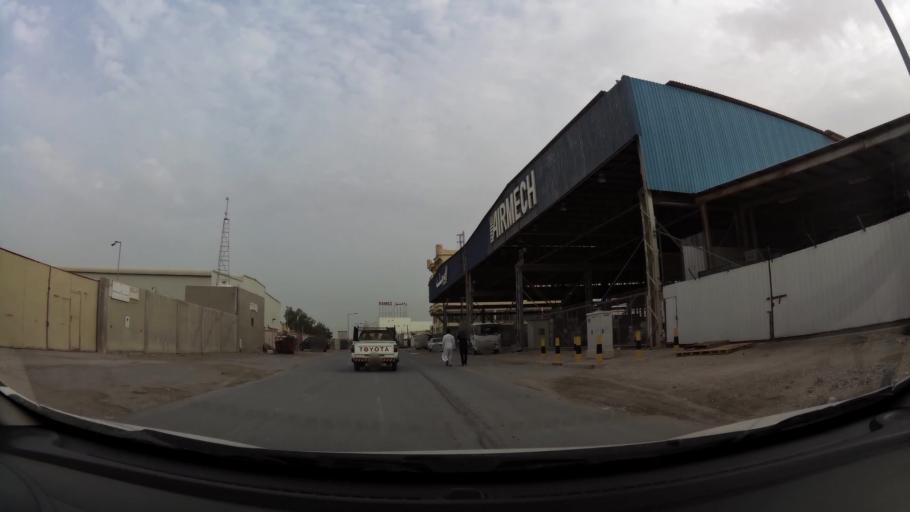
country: BH
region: Northern
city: Ar Rifa'
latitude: 26.1262
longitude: 50.5871
